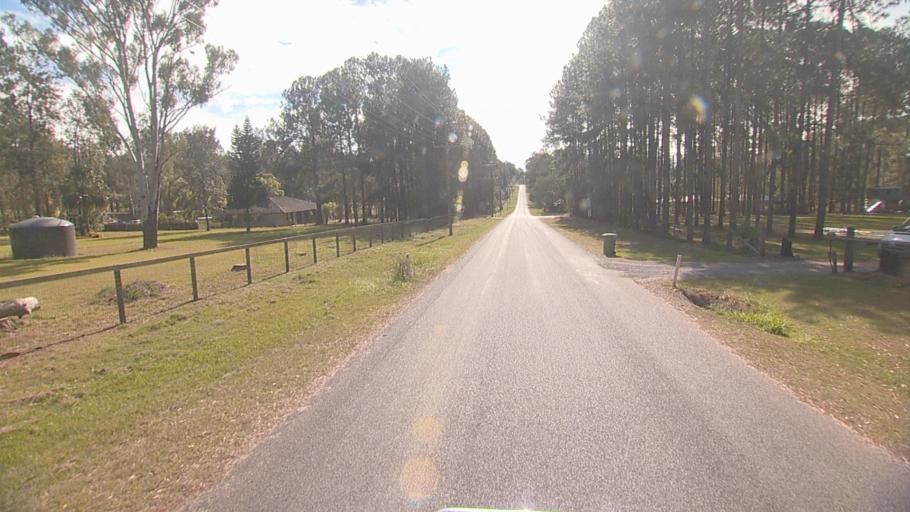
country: AU
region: Queensland
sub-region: Logan
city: North Maclean
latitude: -27.7768
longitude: 152.9911
